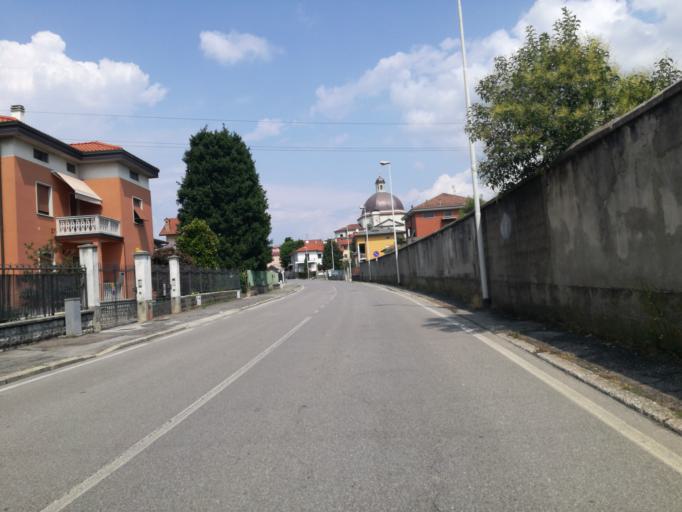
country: IT
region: Lombardy
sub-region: Provincia di Bergamo
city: Calusco d'Adda
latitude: 45.6853
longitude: 9.4731
